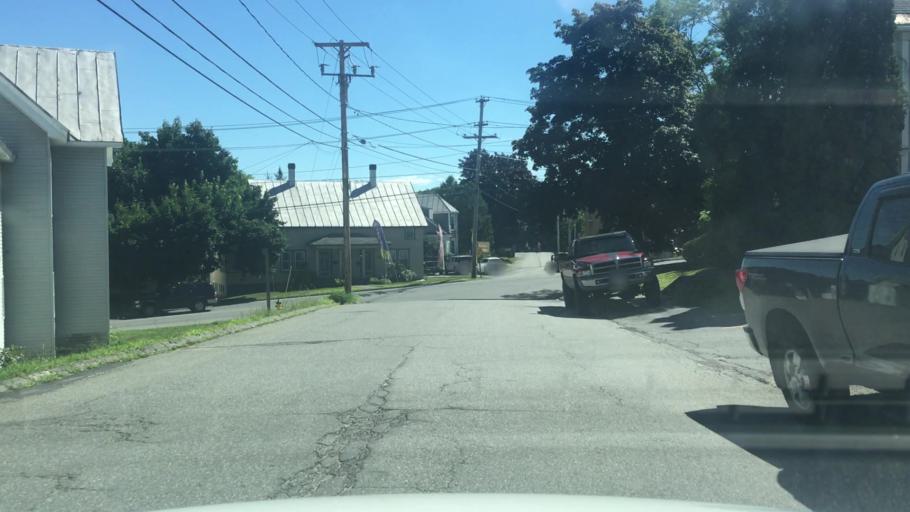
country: US
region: Maine
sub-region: Kennebec County
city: Waterville
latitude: 44.5487
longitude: -69.6415
